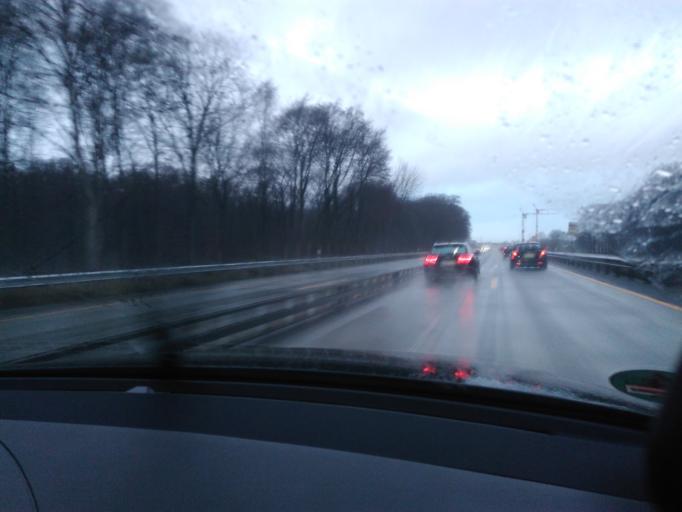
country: DE
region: Schleswig-Holstein
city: Bimohlen
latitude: 53.9321
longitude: 9.9436
